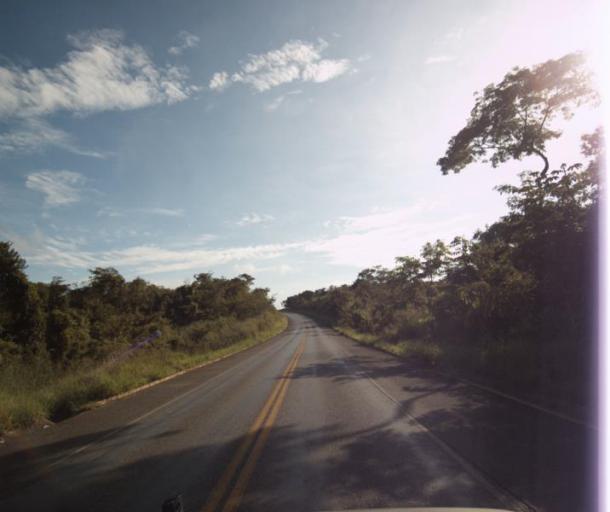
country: BR
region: Goias
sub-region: Pirenopolis
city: Pirenopolis
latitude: -15.5718
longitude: -48.6228
